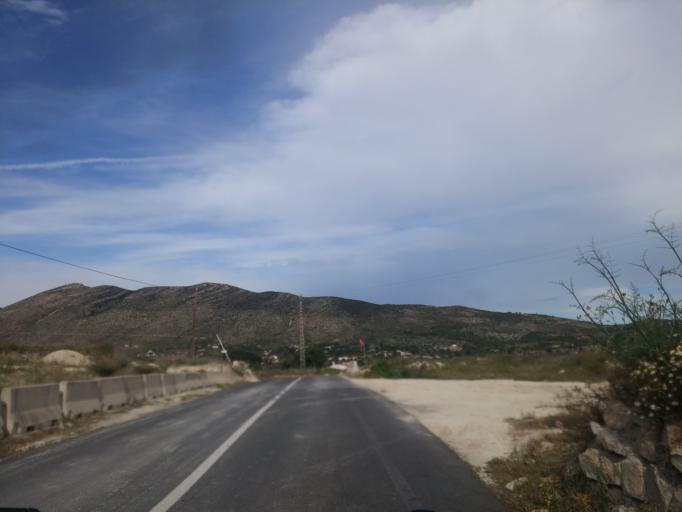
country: ES
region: Valencia
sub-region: Provincia de Alicante
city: Benissa
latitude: 38.7105
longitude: 0.0365
